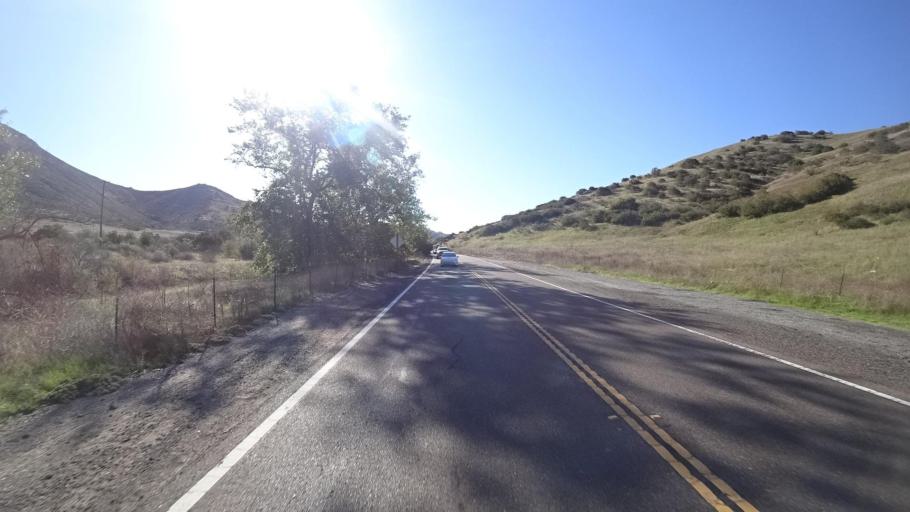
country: US
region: California
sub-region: San Diego County
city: Jamul
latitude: 32.6617
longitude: -116.8122
